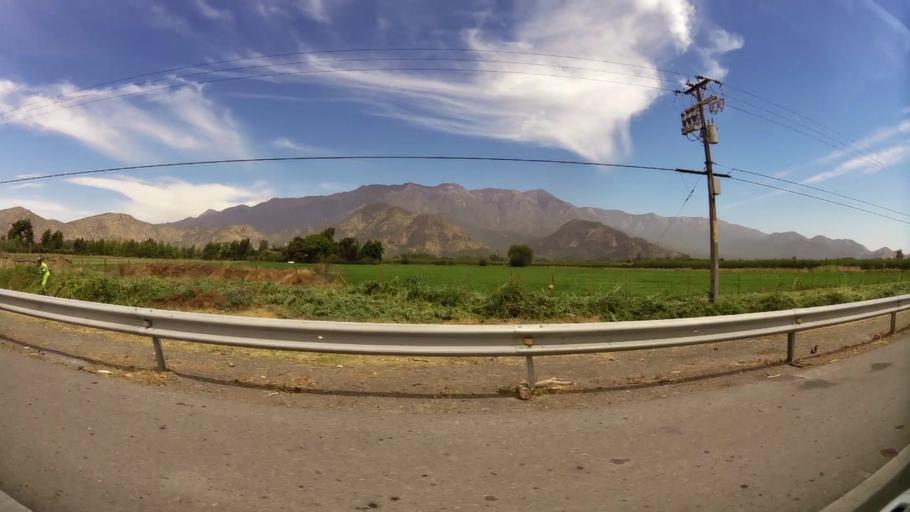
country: CL
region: O'Higgins
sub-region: Provincia de Cachapoal
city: Graneros
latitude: -34.0054
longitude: -70.7031
